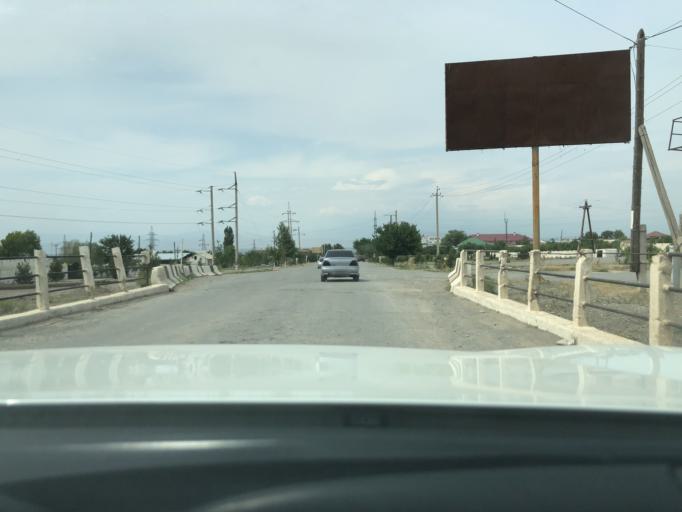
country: TJ
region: Viloyati Sughd
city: Konibodom
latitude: 40.2742
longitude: 70.4462
